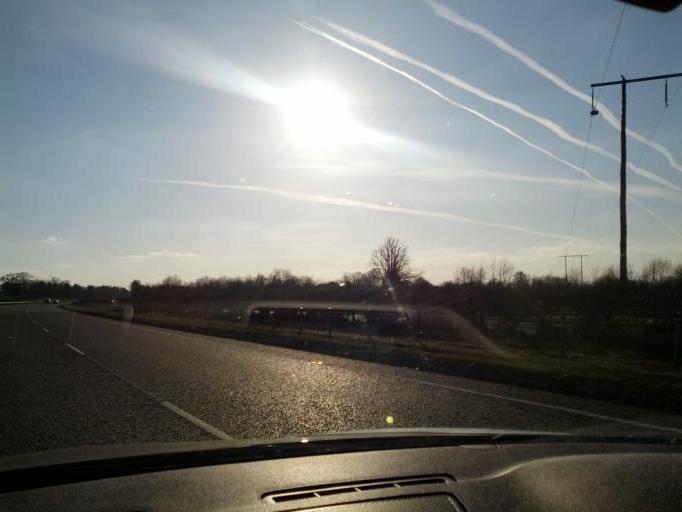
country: IE
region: Leinster
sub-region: Laois
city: Portlaoise
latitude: 53.0188
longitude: -7.2649
